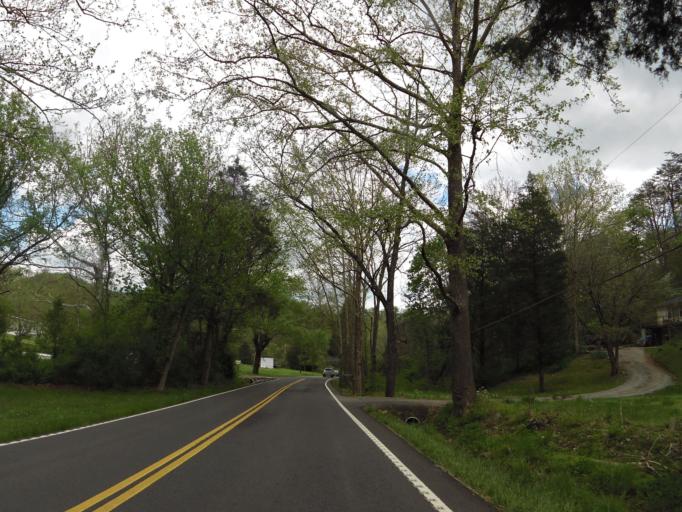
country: US
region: Tennessee
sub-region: Anderson County
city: Norris
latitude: 36.1242
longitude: -83.9980
